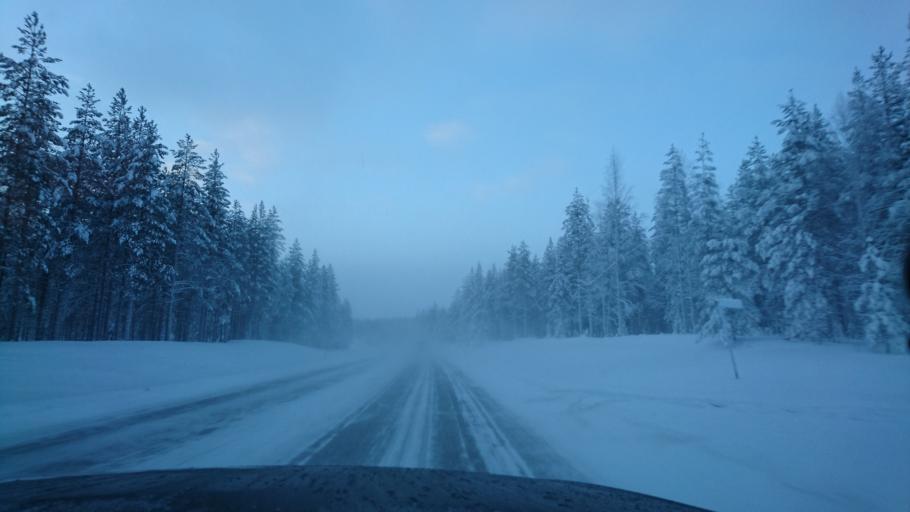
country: FI
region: Northern Ostrobothnia
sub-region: Koillismaa
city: Taivalkoski
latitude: 65.4837
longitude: 27.8094
